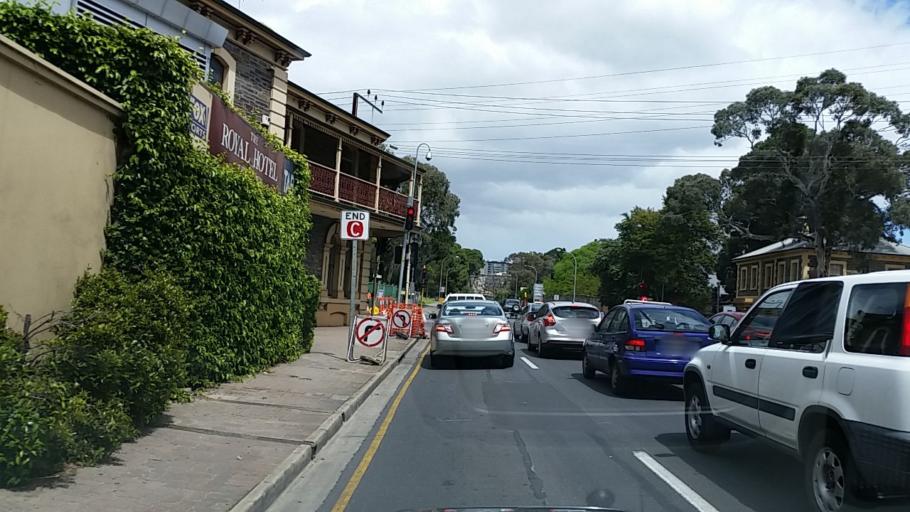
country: AU
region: South Australia
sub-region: Adelaide
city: Adelaide
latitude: -34.9194
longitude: 138.6156
